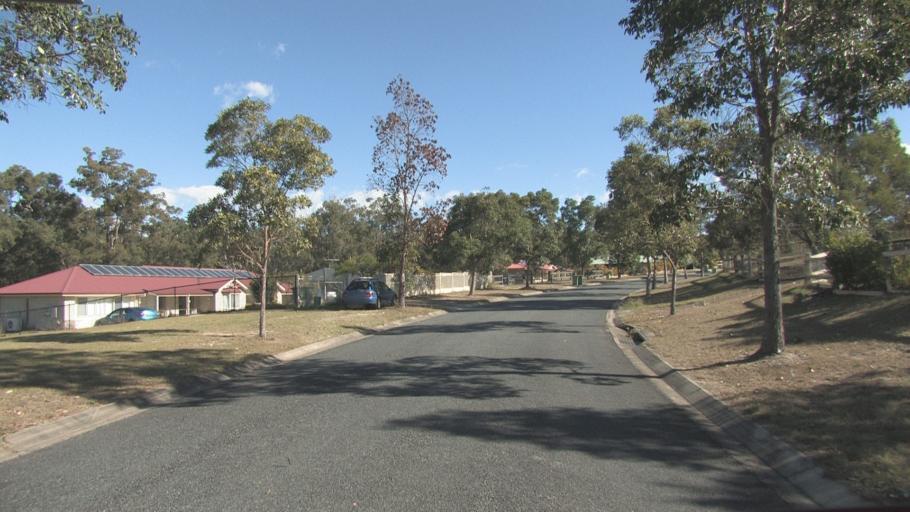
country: AU
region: Queensland
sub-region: Ipswich
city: Springfield Lakes
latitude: -27.7347
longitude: 152.9122
